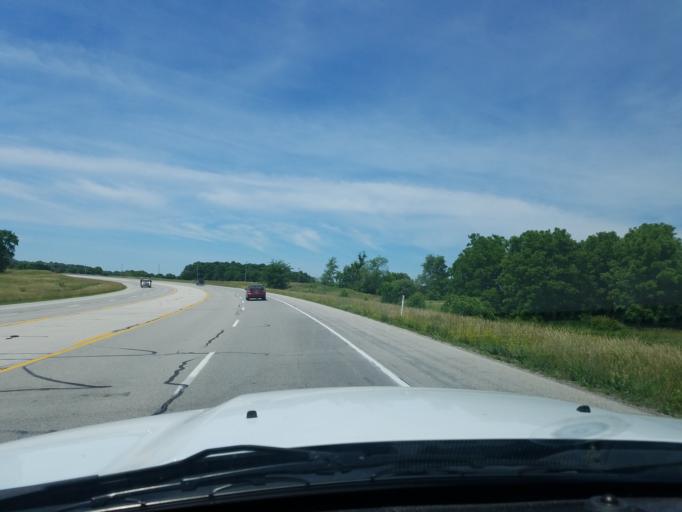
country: US
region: Indiana
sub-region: Delaware County
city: Yorktown
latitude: 40.1208
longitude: -85.4731
